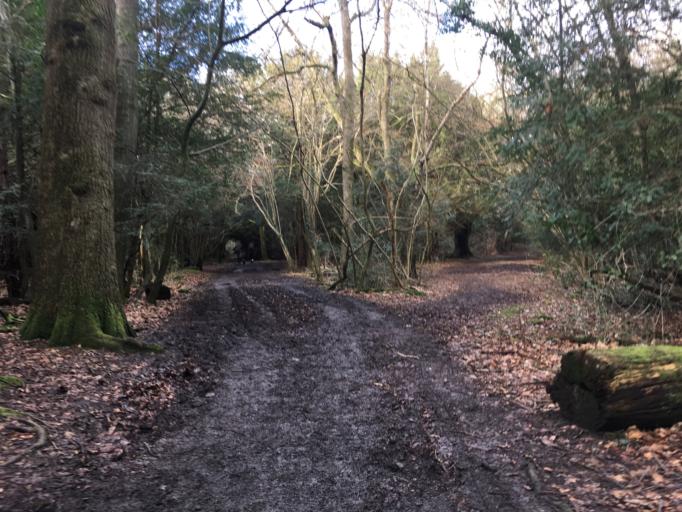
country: GB
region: England
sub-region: Surrey
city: Mickleham
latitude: 51.2502
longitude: -0.3015
